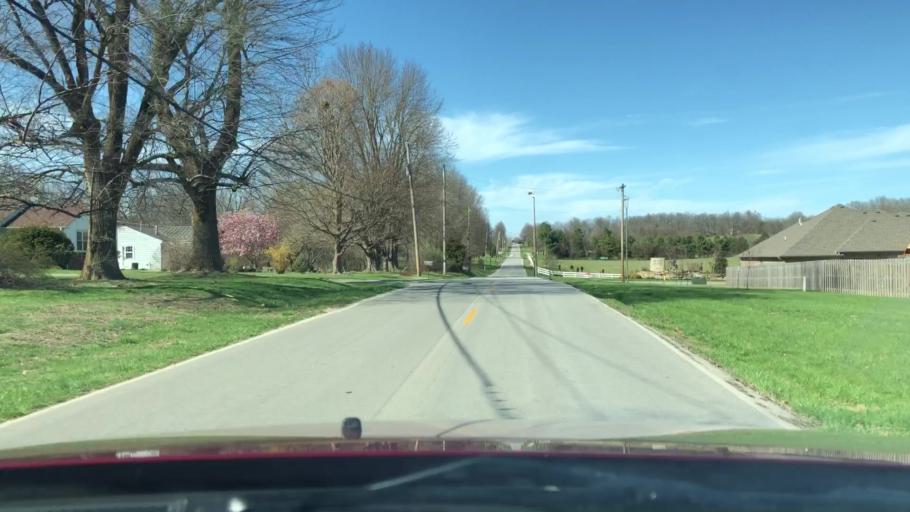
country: US
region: Missouri
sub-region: Greene County
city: Strafford
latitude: 37.2310
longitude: -93.1884
